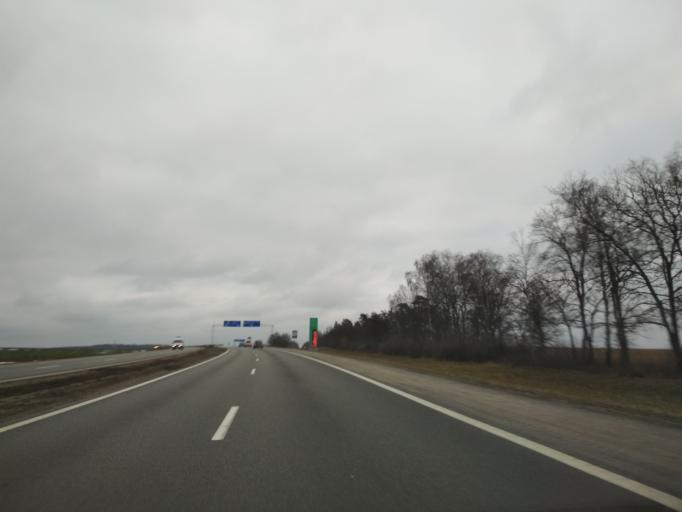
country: BY
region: Minsk
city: Blon'
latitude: 53.5509
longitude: 28.1600
